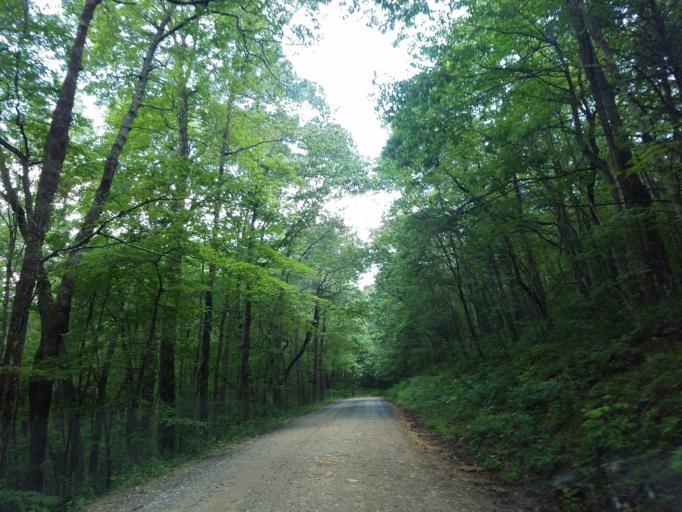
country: US
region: Georgia
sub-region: Fannin County
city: Blue Ridge
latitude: 34.6514
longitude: -84.2166
